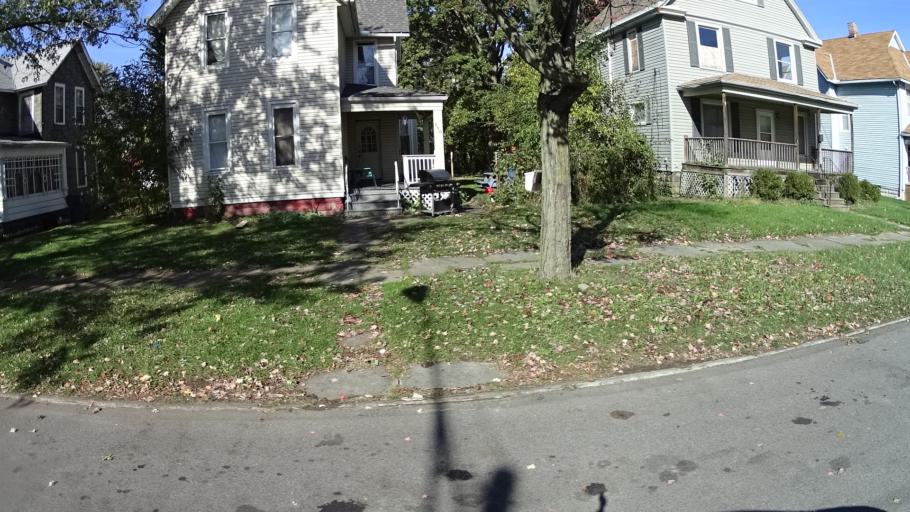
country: US
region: Ohio
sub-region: Lorain County
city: Lorain
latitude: 41.4618
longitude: -82.1758
